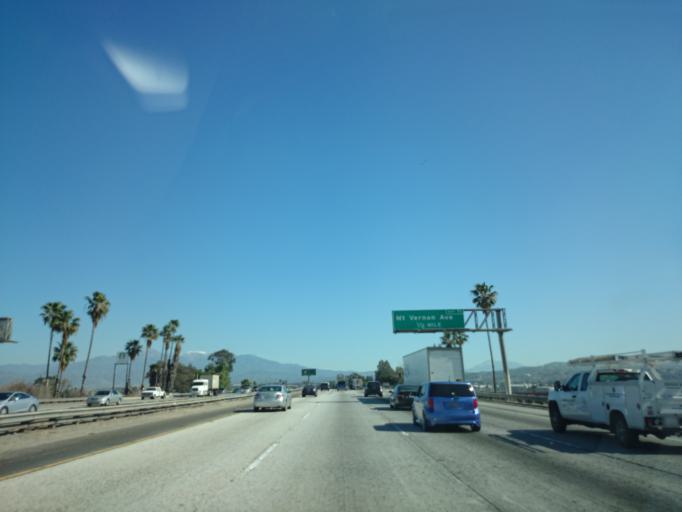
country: US
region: California
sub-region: San Bernardino County
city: Colton
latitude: 34.0658
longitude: -117.3240
